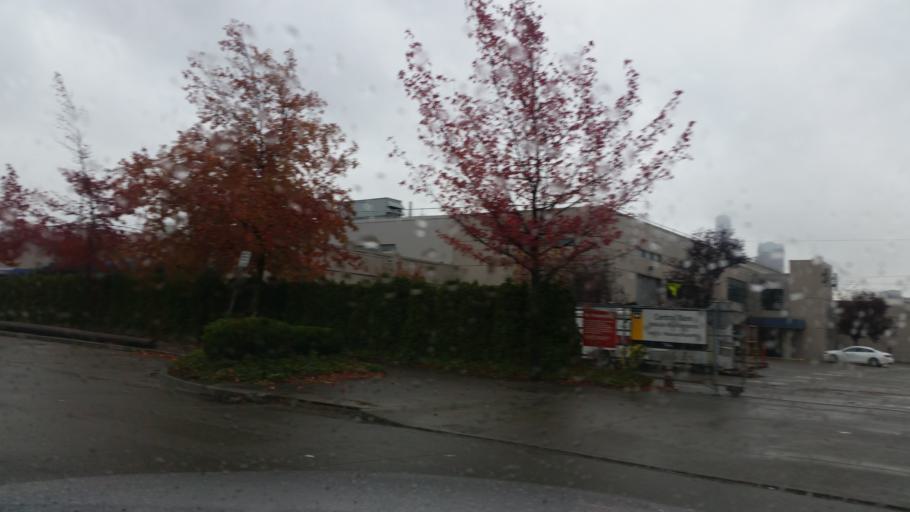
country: US
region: Washington
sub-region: King County
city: Seattle
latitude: 47.5882
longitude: -122.3235
